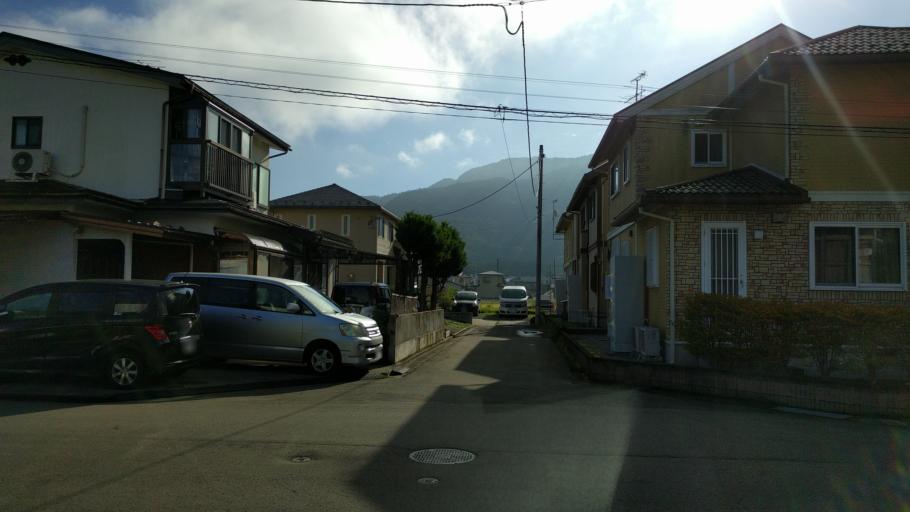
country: JP
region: Fukushima
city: Kitakata
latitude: 37.4721
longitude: 139.9298
